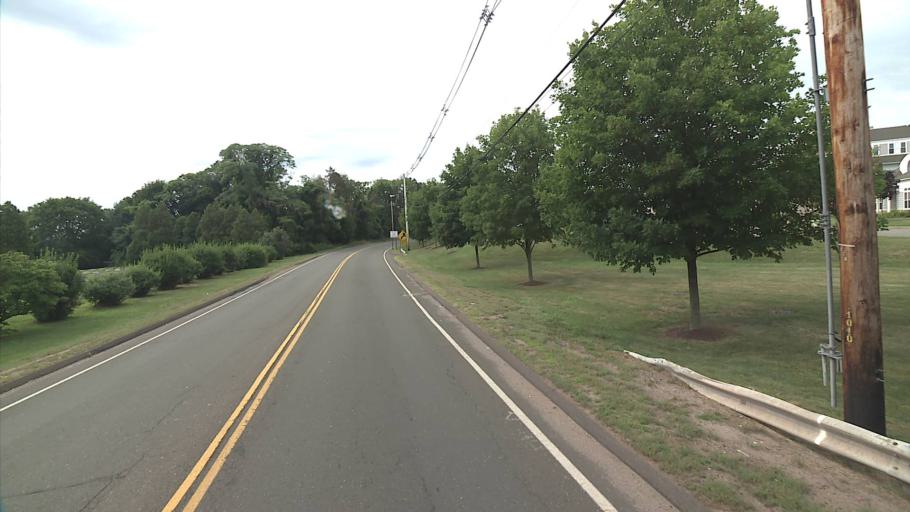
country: US
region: Connecticut
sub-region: New Haven County
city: Wallingford
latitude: 41.4648
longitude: -72.8342
